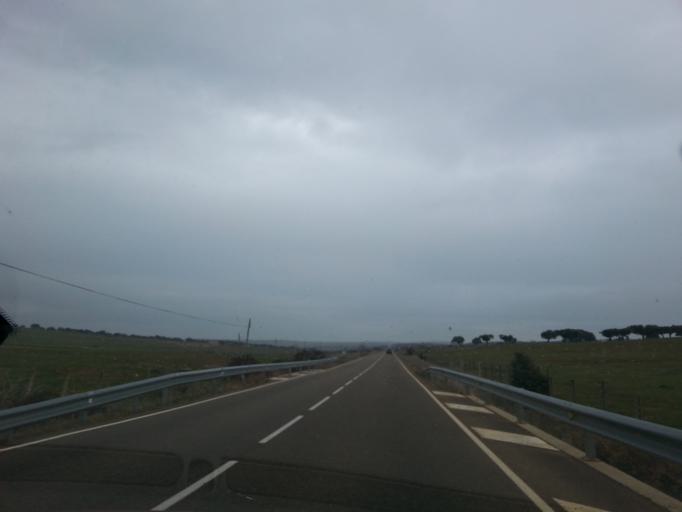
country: ES
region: Castille and Leon
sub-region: Provincia de Salamanca
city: Tamames
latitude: 40.6695
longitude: -6.0798
